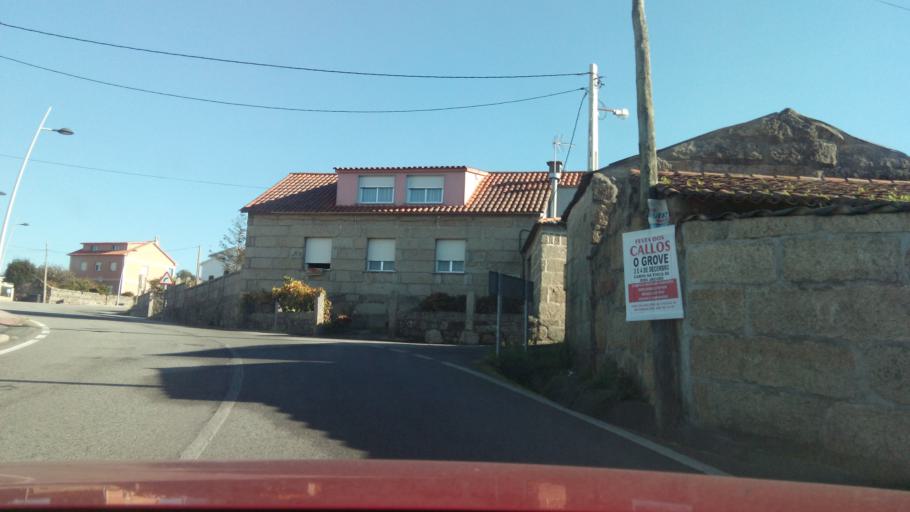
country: ES
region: Galicia
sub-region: Provincia de Pontevedra
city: O Grove
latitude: 42.4682
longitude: -8.9059
